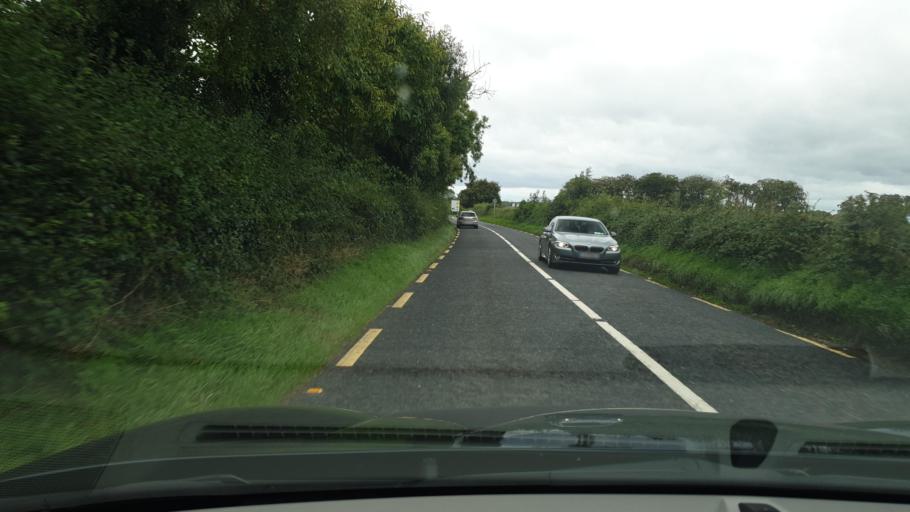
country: IE
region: Leinster
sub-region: Kildare
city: Naas
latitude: 53.2232
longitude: -6.7093
